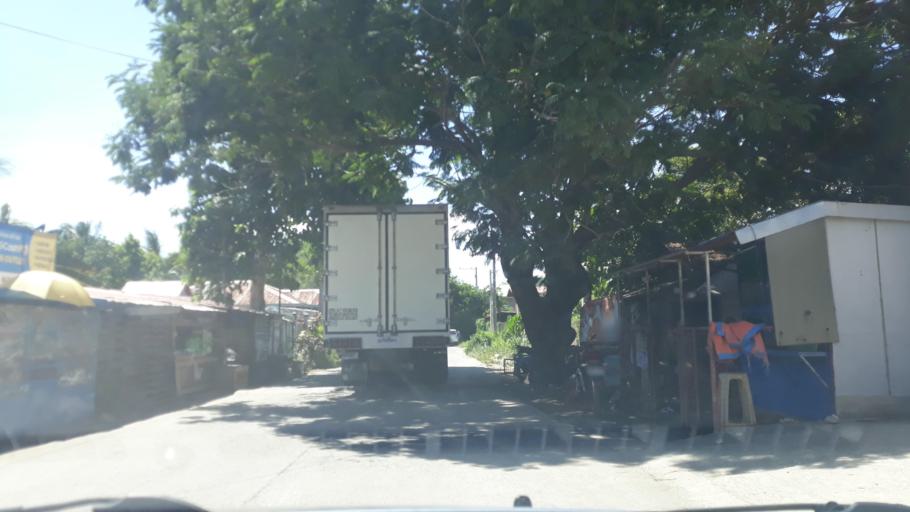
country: PH
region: Calabarzon
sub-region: Province of Cavite
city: Manggahan
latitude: 14.2994
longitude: 120.9168
